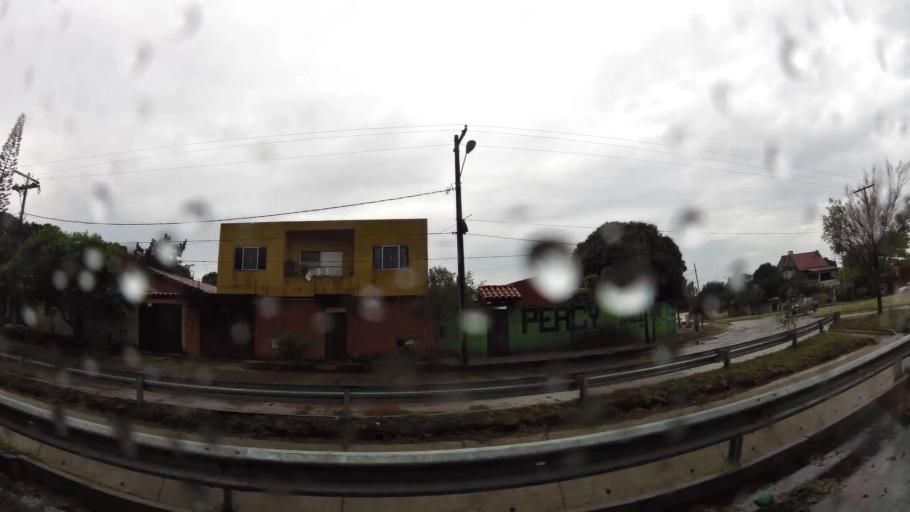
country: BO
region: Santa Cruz
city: Santa Cruz de la Sierra
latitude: -17.8019
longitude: -63.1594
